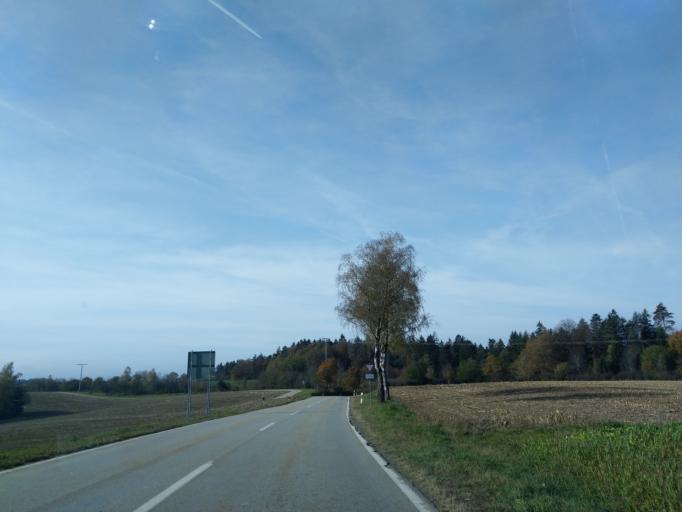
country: DE
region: Bavaria
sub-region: Lower Bavaria
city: Auerbach
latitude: 48.8139
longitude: 13.1220
